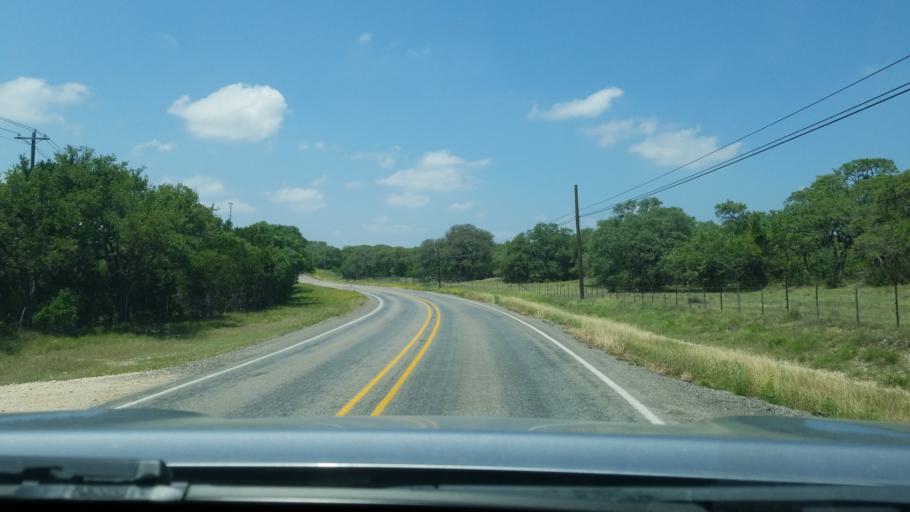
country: US
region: Texas
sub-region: Hays County
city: Woodcreek
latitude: 30.0428
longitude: -98.1926
